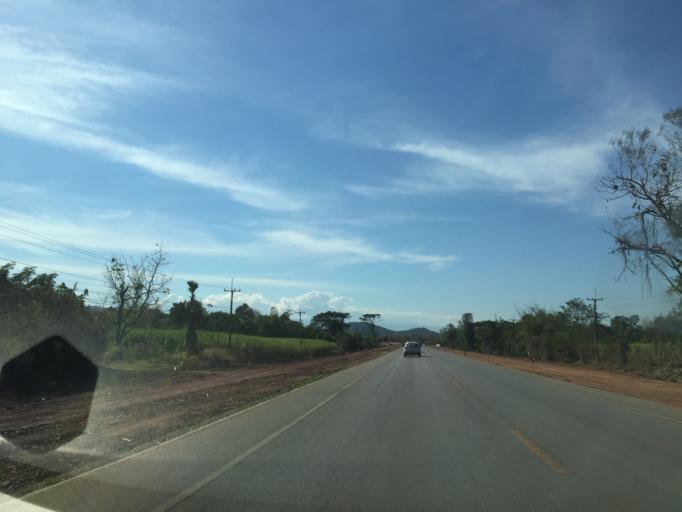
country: TH
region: Loei
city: Erawan
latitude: 17.2989
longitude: 101.8639
